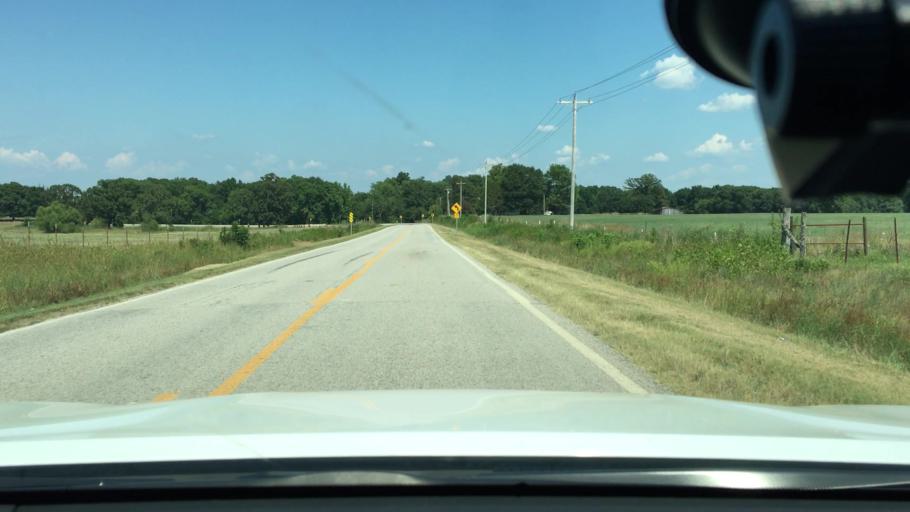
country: US
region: Arkansas
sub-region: Johnson County
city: Coal Hill
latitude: 35.3507
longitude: -93.5710
